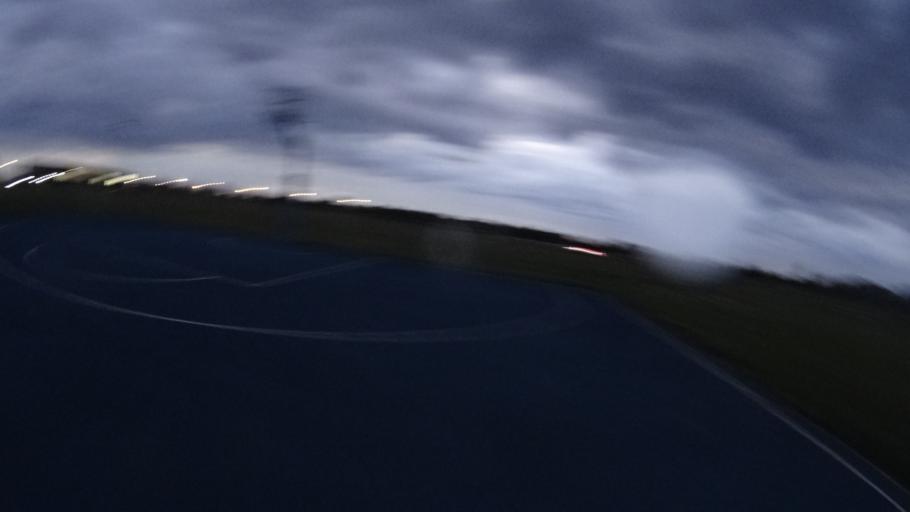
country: PL
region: Masovian Voivodeship
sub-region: Powiat warszawski zachodni
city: Ozarow Mazowiecki
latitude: 52.2332
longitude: 20.7998
